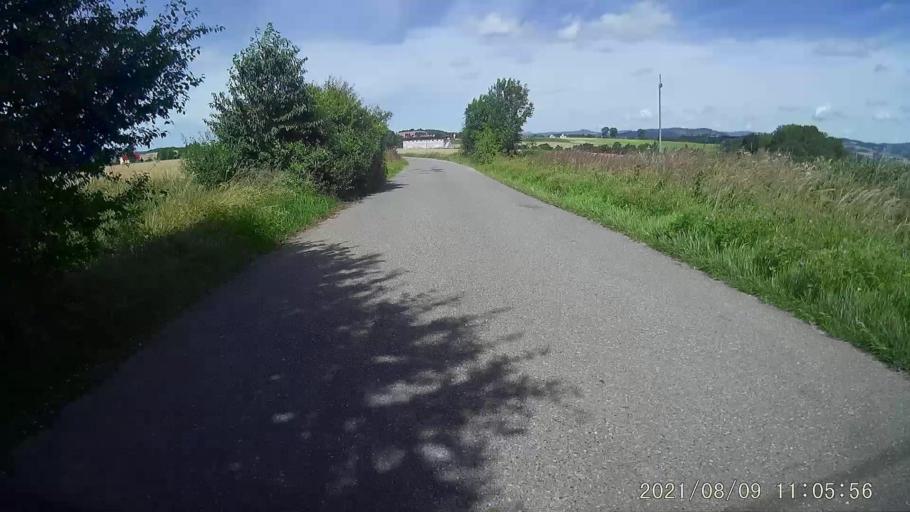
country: PL
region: Lower Silesian Voivodeship
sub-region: Powiat klodzki
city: Bozkow
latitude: 50.4583
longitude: 16.5843
